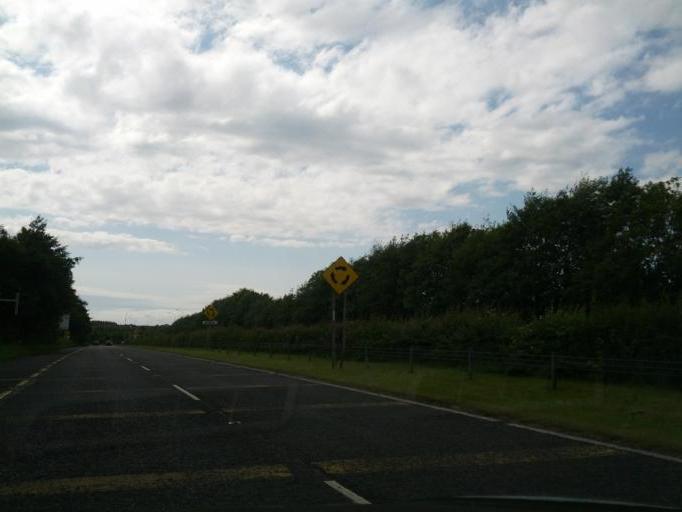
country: IE
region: Connaught
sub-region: County Galway
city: Oranmore
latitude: 53.2790
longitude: -8.9680
